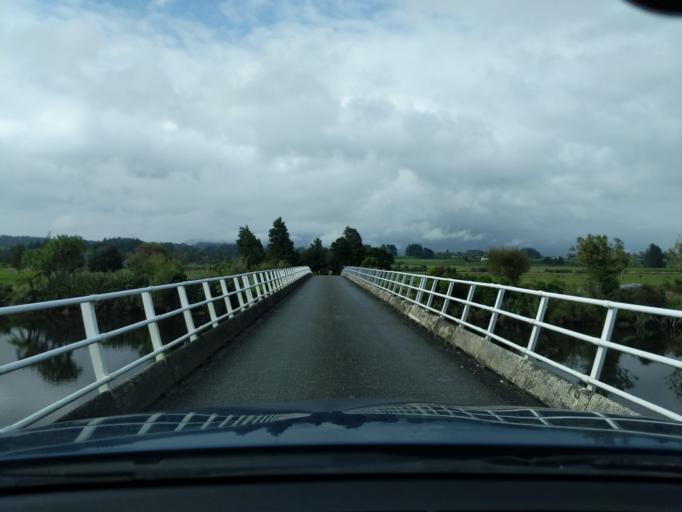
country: NZ
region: Tasman
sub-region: Tasman District
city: Takaka
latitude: -40.6751
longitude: 172.6612
